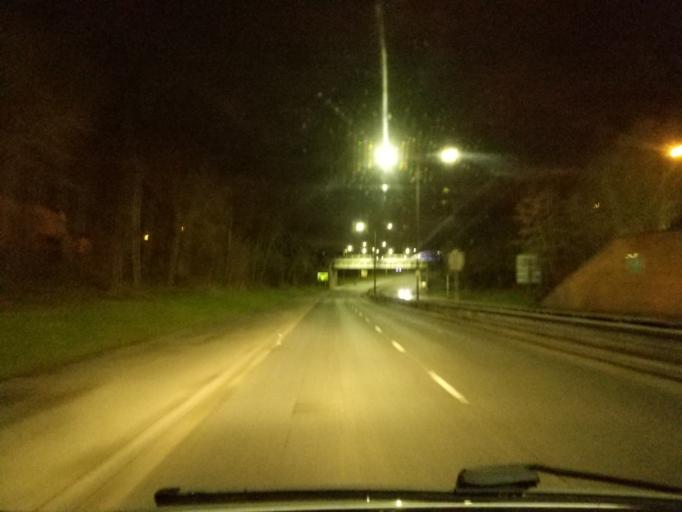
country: GB
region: England
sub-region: St. Helens
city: St Helens
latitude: 53.4505
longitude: -2.7282
